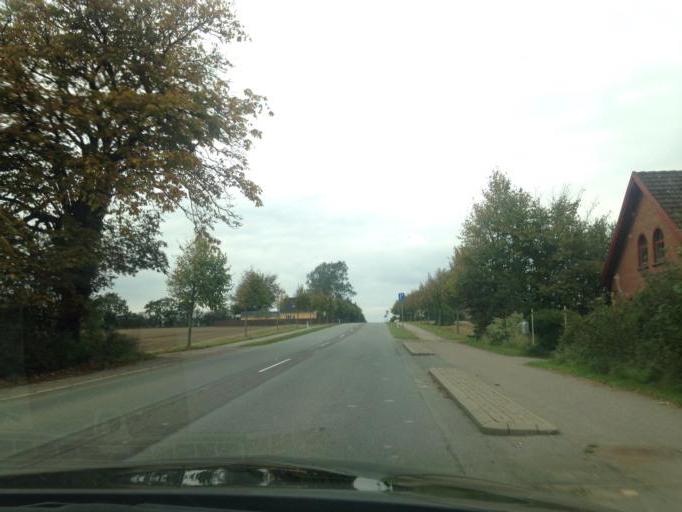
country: DK
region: South Denmark
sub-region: Kolding Kommune
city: Christiansfeld
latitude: 55.3859
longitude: 9.4802
